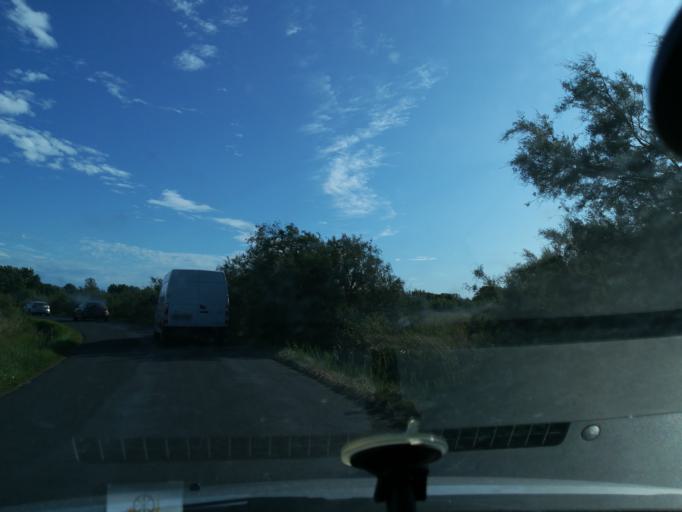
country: FR
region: Languedoc-Roussillon
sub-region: Departement de l'Herault
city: Vias
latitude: 43.2940
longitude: 3.3908
